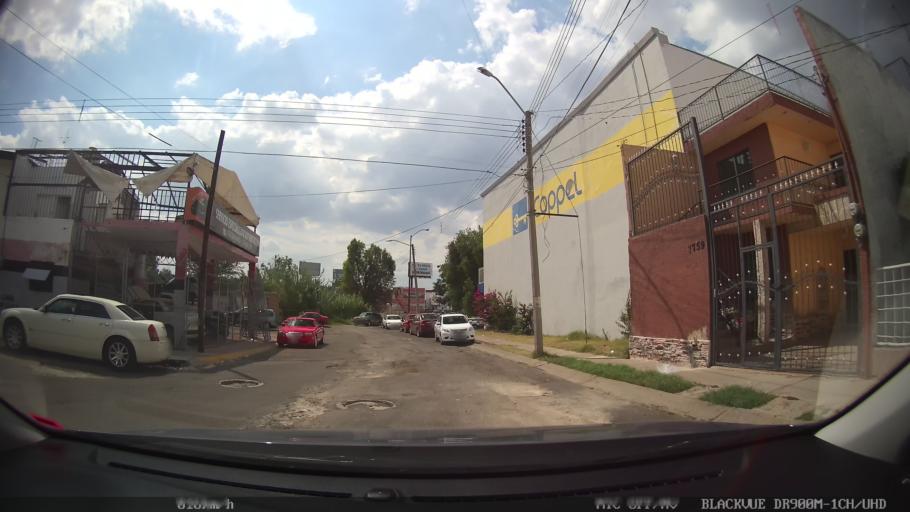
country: MX
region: Jalisco
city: Tlaquepaque
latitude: 20.6307
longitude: -103.2668
